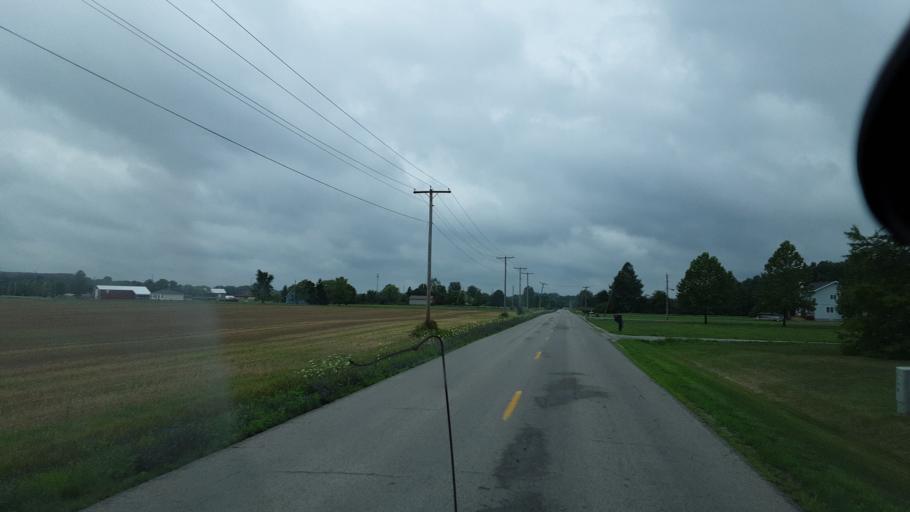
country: US
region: Indiana
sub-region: Allen County
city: New Haven
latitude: 40.9470
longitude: -85.0431
